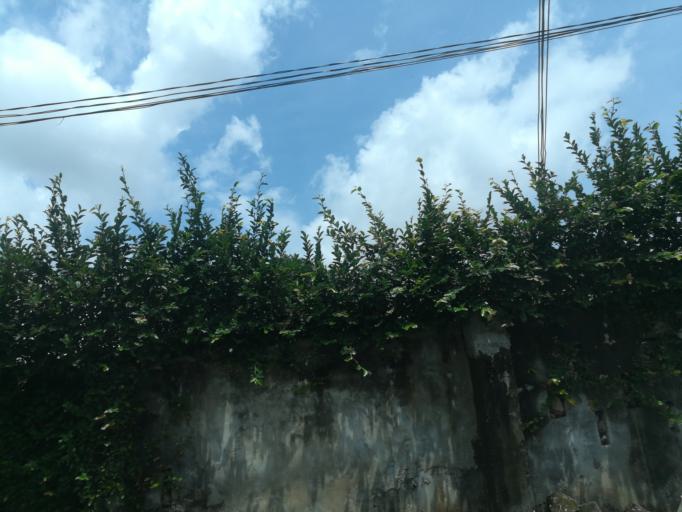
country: NG
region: Lagos
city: Somolu
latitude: 6.5412
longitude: 3.3636
